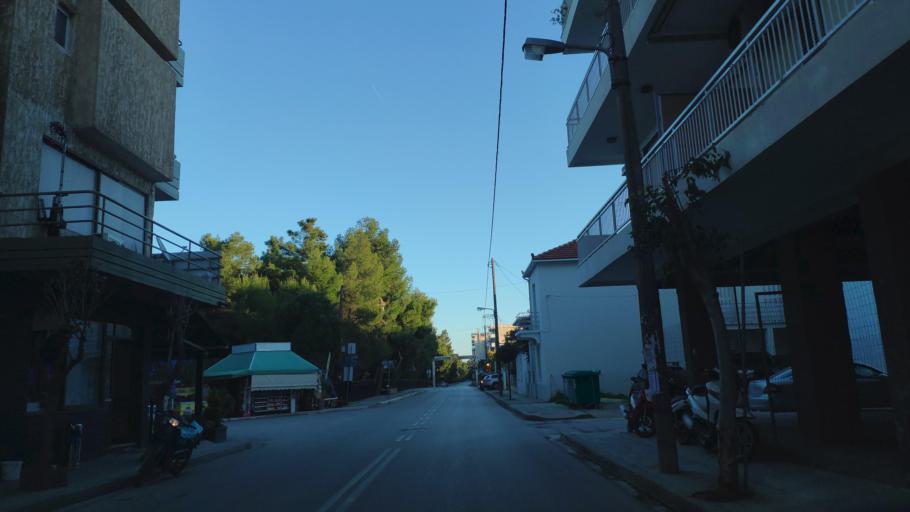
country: GR
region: Peloponnese
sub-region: Nomos Korinthias
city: Xylokastro
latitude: 38.0761
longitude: 22.6375
